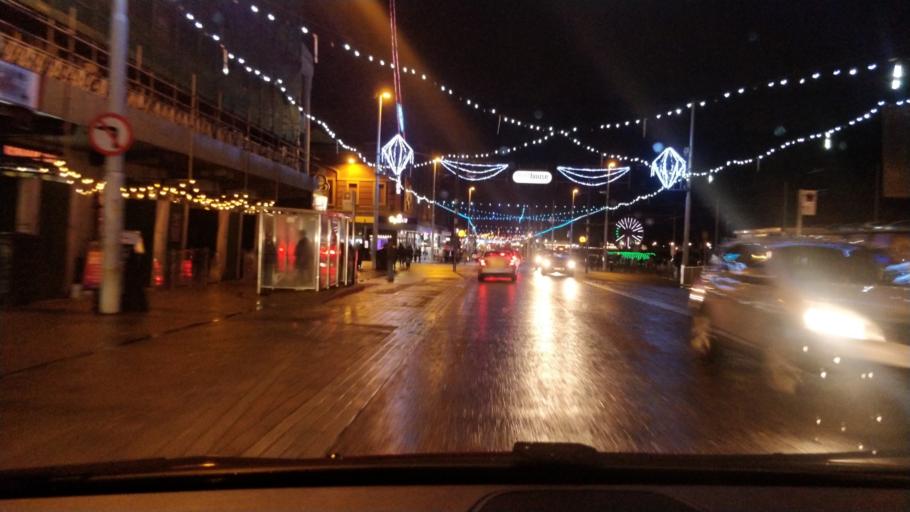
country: GB
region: England
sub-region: Blackpool
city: Blackpool
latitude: 53.8180
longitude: -3.0558
